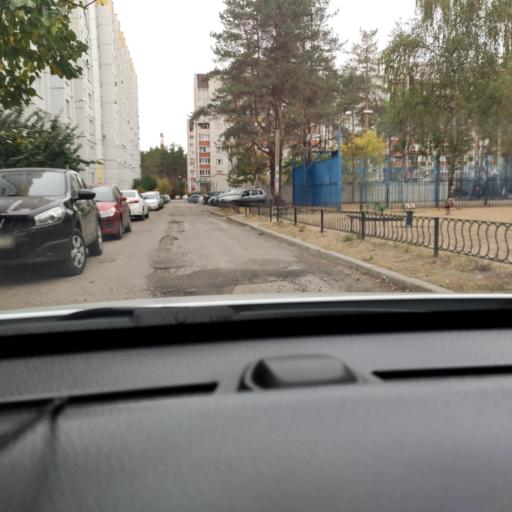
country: RU
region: Voronezj
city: Voronezh
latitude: 51.6873
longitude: 39.2811
